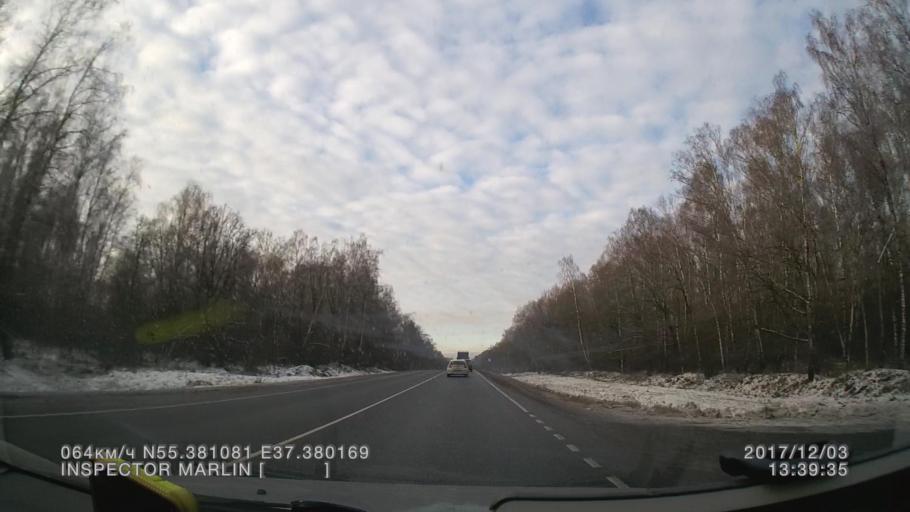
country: RU
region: Moskovskaya
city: Dubrovitsy
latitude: 55.3811
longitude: 37.3801
